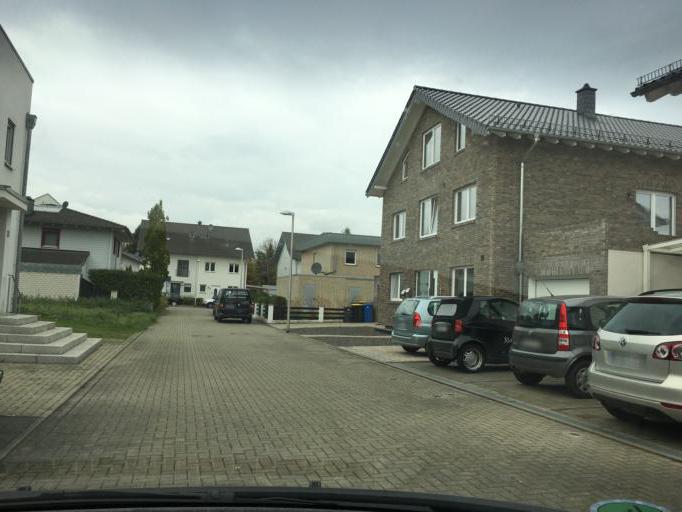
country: DE
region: North Rhine-Westphalia
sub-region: Regierungsbezirk Koln
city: Dueren
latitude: 50.7978
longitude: 6.4728
